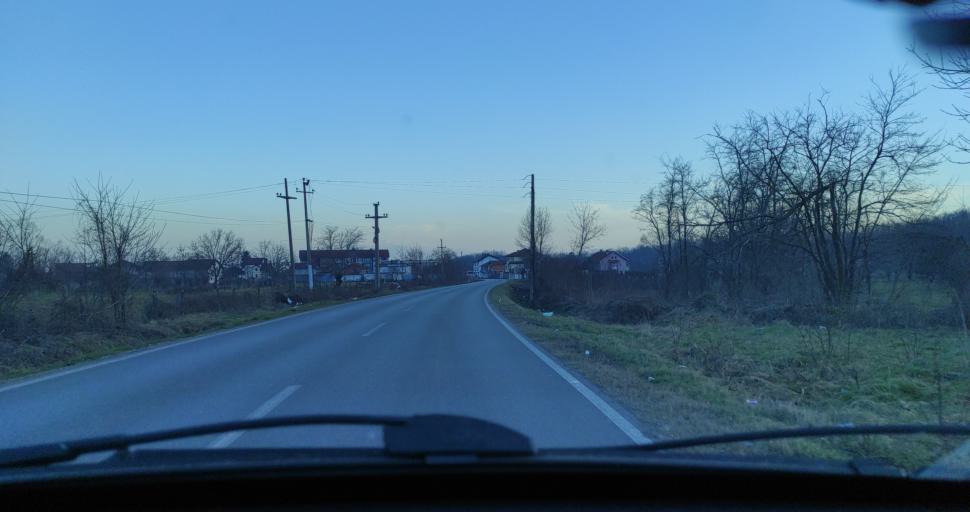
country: XK
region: Gjakova
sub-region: Komuna e Decanit
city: Prilep
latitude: 42.5083
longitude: 20.3111
